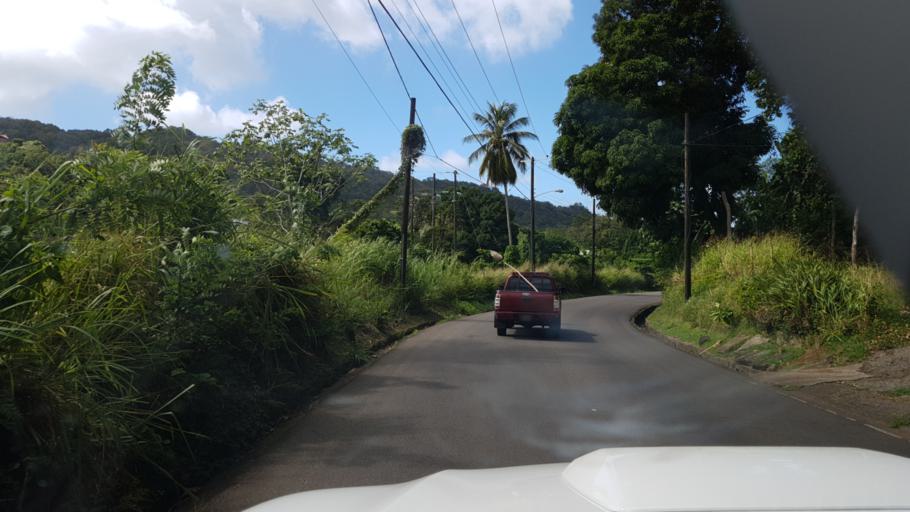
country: LC
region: Castries Quarter
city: Bisee
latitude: 14.0183
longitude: -60.9590
